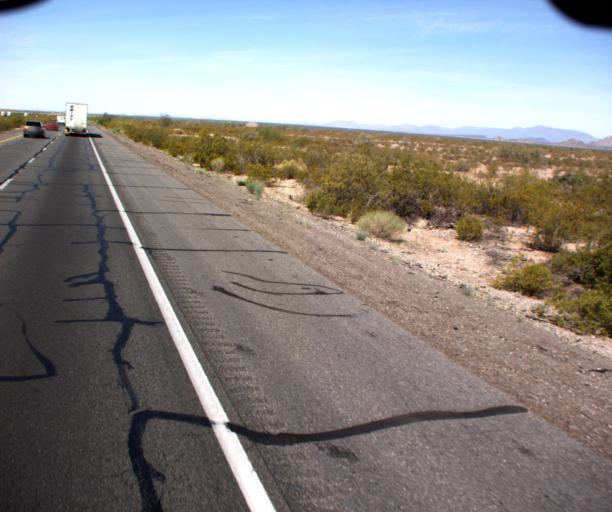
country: US
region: Arizona
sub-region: La Paz County
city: Salome
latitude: 33.5305
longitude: -113.1224
